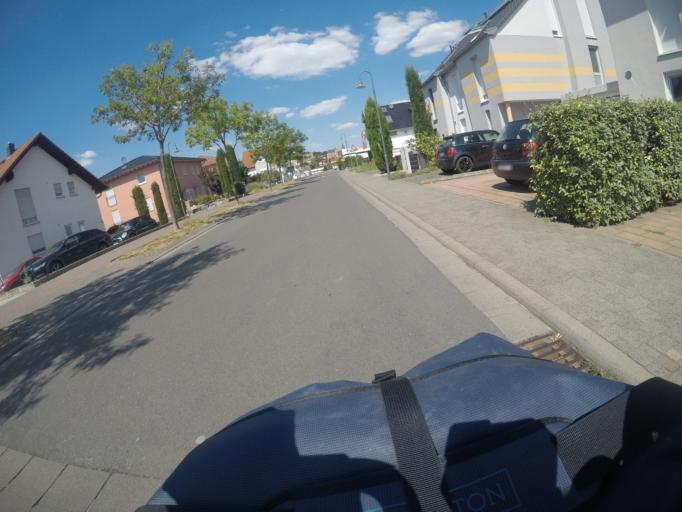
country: DE
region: Rheinland-Pfalz
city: Dienheim
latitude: 49.8433
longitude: 8.3538
